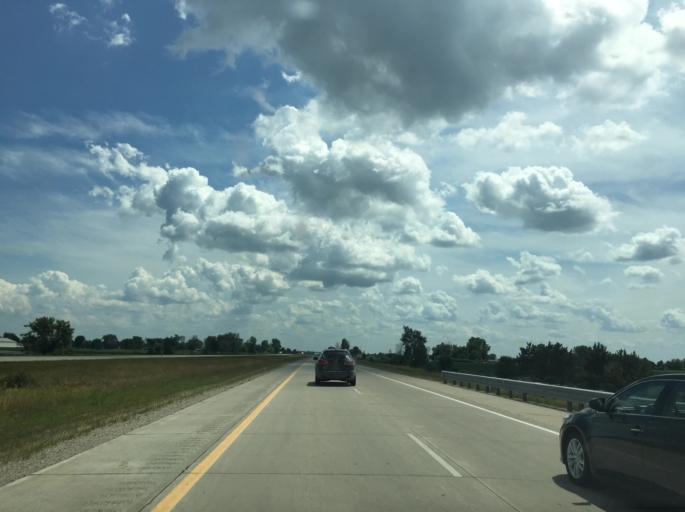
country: US
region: Michigan
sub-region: Bay County
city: Pinconning
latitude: 43.8174
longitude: -84.0207
